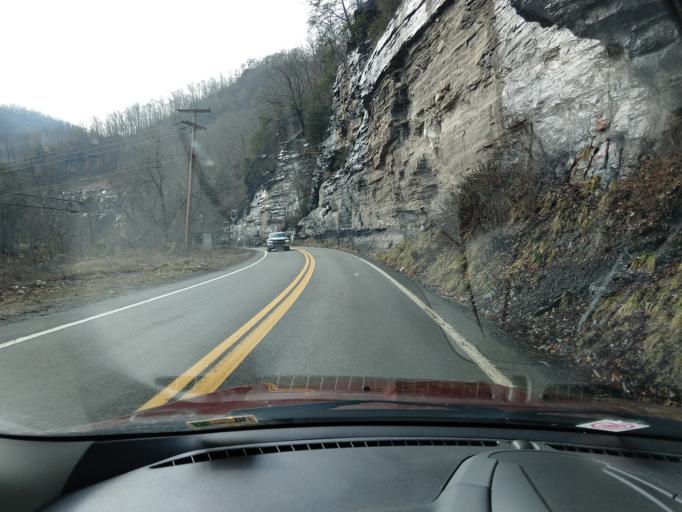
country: US
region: West Virginia
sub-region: McDowell County
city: Welch
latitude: 37.3627
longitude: -81.8010
